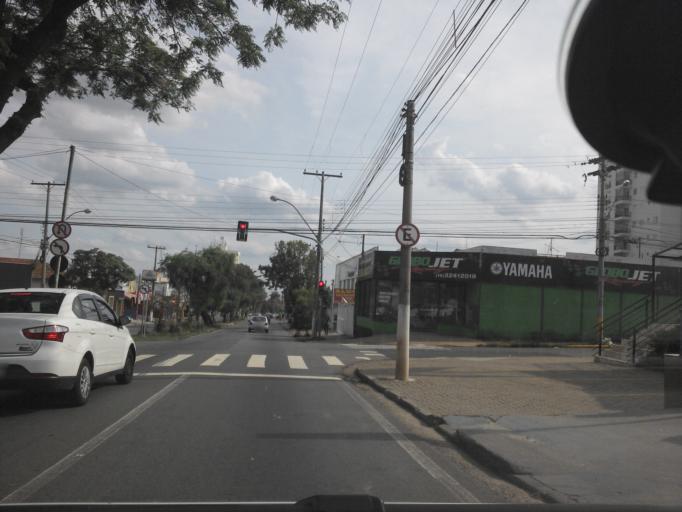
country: BR
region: Sao Paulo
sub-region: Campinas
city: Campinas
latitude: -22.8927
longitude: -47.0780
